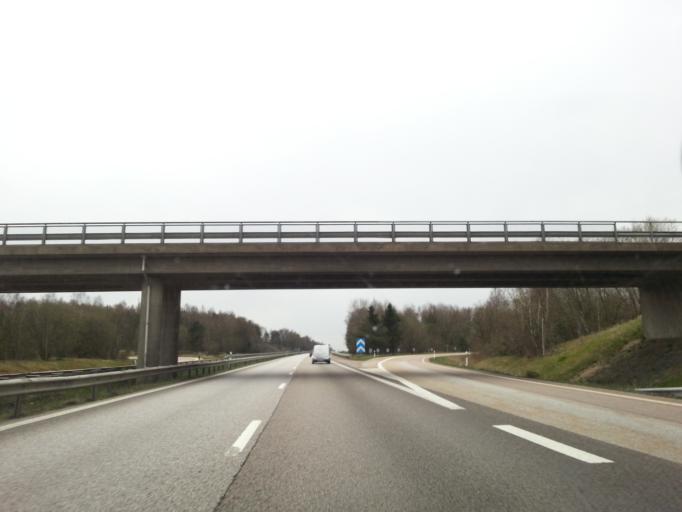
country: SE
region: Skane
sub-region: Bastads Kommun
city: Bastad
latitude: 56.3950
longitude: 12.9412
